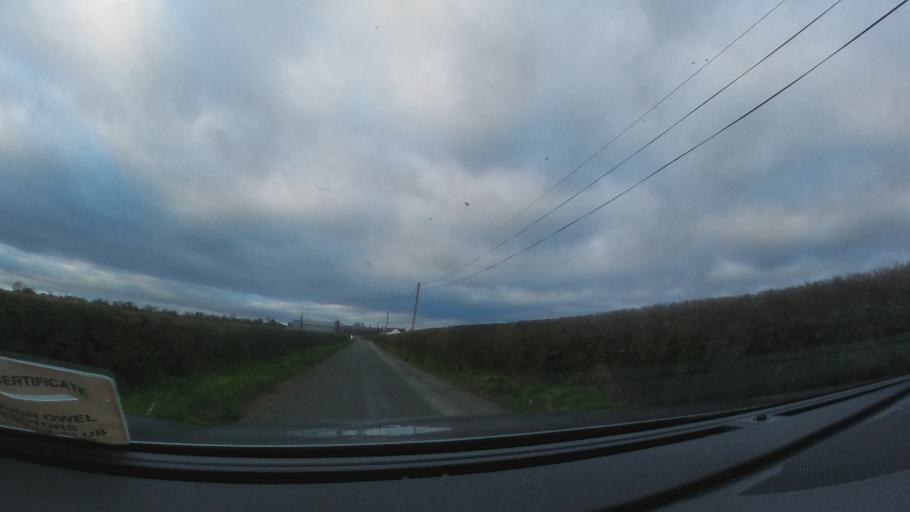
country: IE
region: Leinster
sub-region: Kilkenny
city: Thomastown
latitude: 52.5831
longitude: -7.1645
